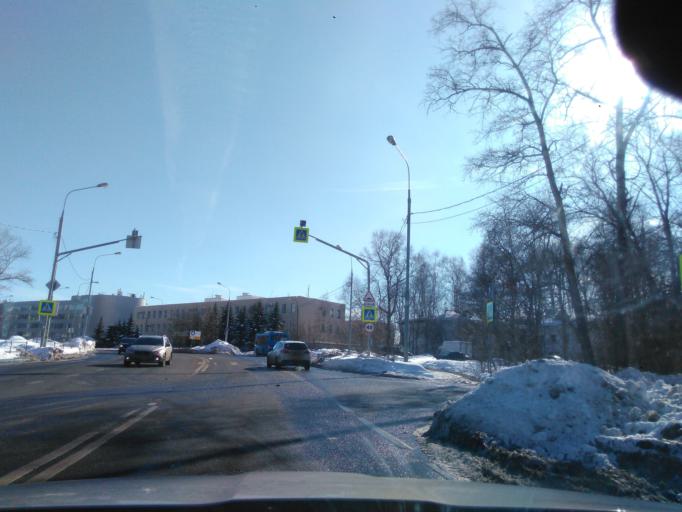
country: RU
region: Moscow
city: Zelenograd
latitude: 55.9856
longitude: 37.1714
